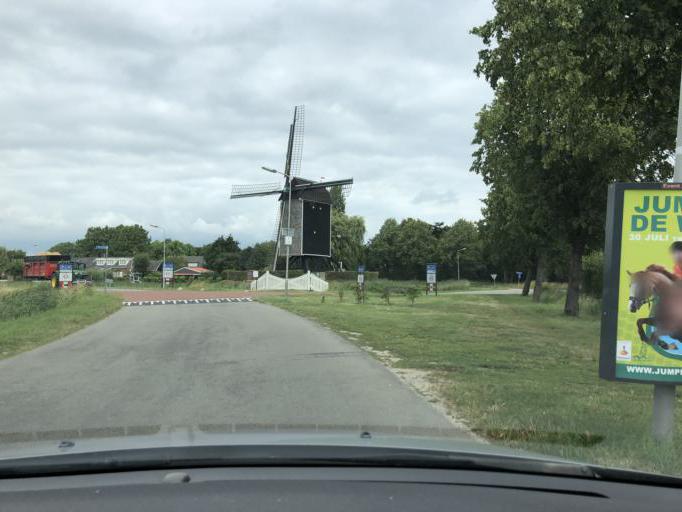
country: NL
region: Zeeland
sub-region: Gemeente Reimerswaal
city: Yerseke
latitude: 51.4239
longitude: 4.0726
